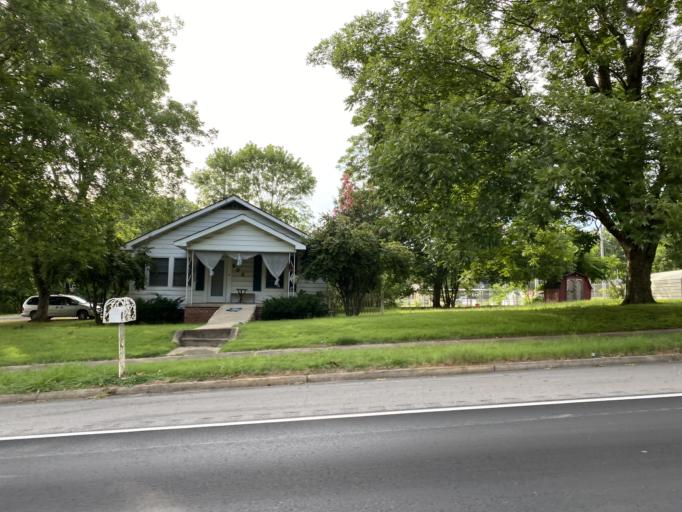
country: US
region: Alabama
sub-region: DeKalb County
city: Fort Payne
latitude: 34.4416
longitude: -85.7140
